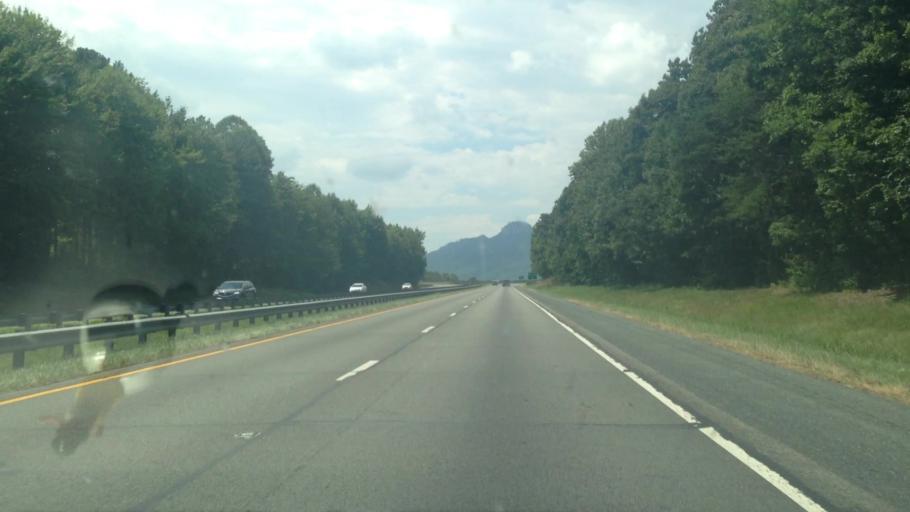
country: US
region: North Carolina
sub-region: Stokes County
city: King
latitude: 36.3132
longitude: -80.4318
